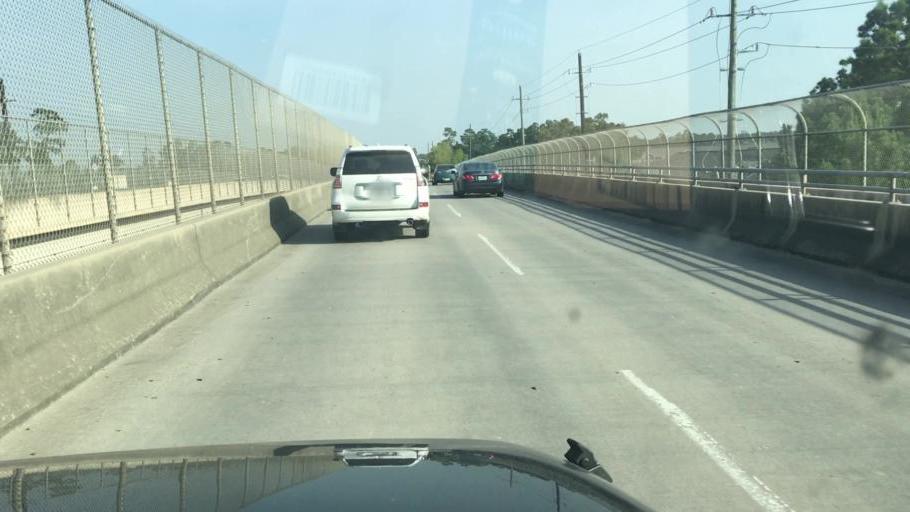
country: US
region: Texas
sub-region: Harris County
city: Atascocita
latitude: 29.9671
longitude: -95.1699
